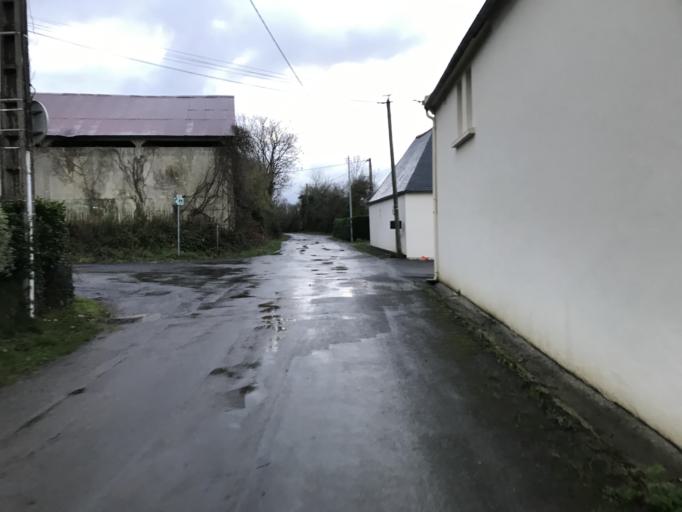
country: FR
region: Brittany
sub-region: Departement du Finistere
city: Plougastel-Daoulas
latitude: 48.3660
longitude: -4.3588
